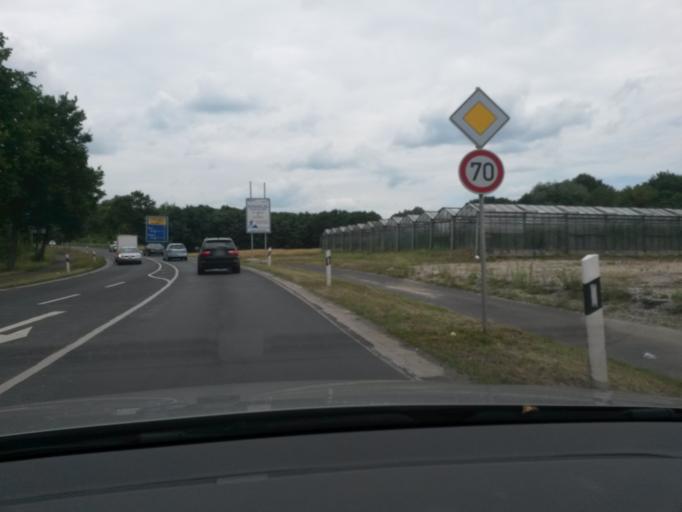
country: DE
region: North Rhine-Westphalia
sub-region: Regierungsbezirk Dusseldorf
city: Nettetal
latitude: 51.2801
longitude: 6.2735
